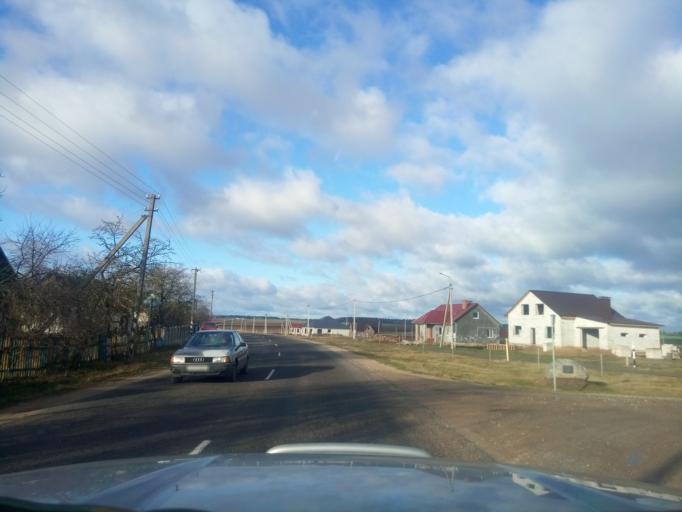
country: BY
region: Minsk
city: Kapyl'
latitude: 53.1602
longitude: 27.0779
